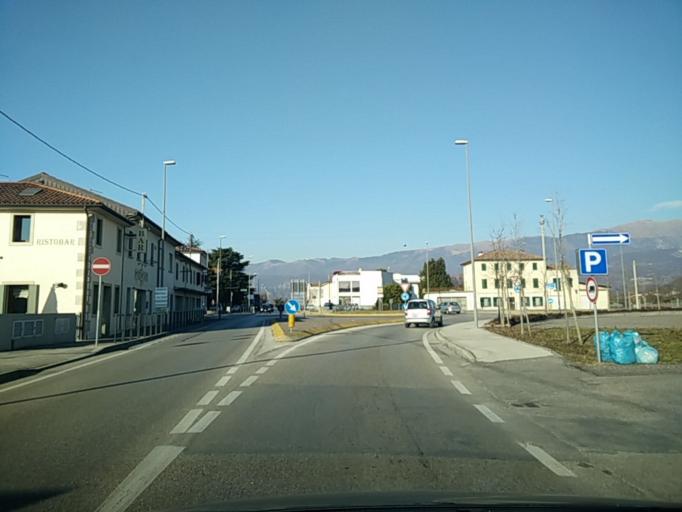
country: IT
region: Veneto
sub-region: Provincia di Treviso
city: Cappella Maggiore
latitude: 45.9571
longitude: 12.3596
